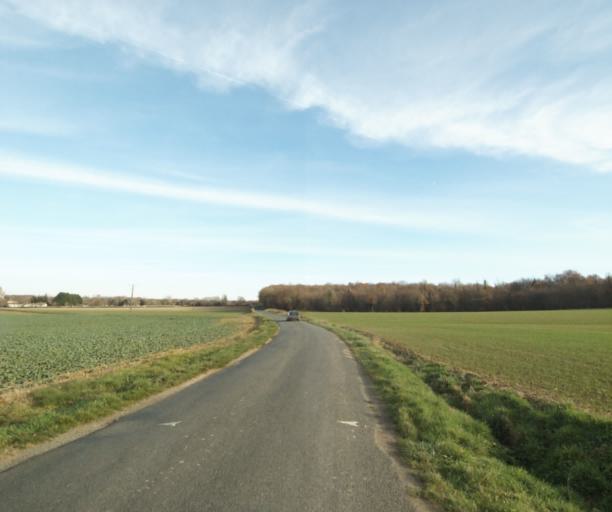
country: FR
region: Poitou-Charentes
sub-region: Departement de la Charente-Maritime
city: Fontcouverte
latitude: 45.8171
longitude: -0.5744
